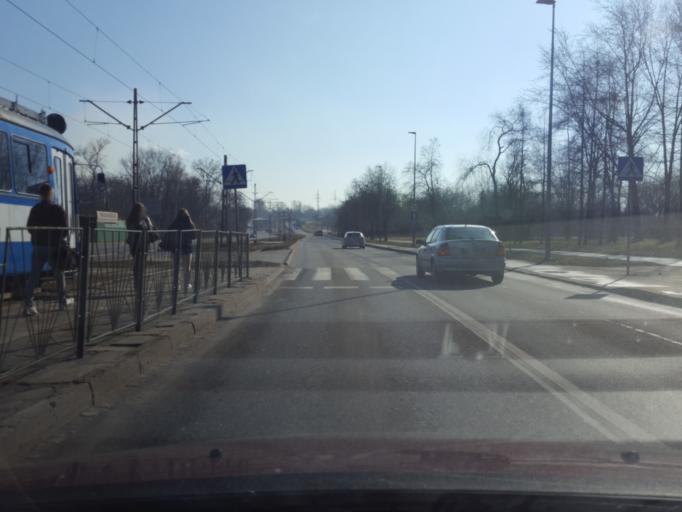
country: PL
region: Lesser Poland Voivodeship
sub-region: Powiat wielicki
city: Kokotow
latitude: 50.0673
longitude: 20.0591
